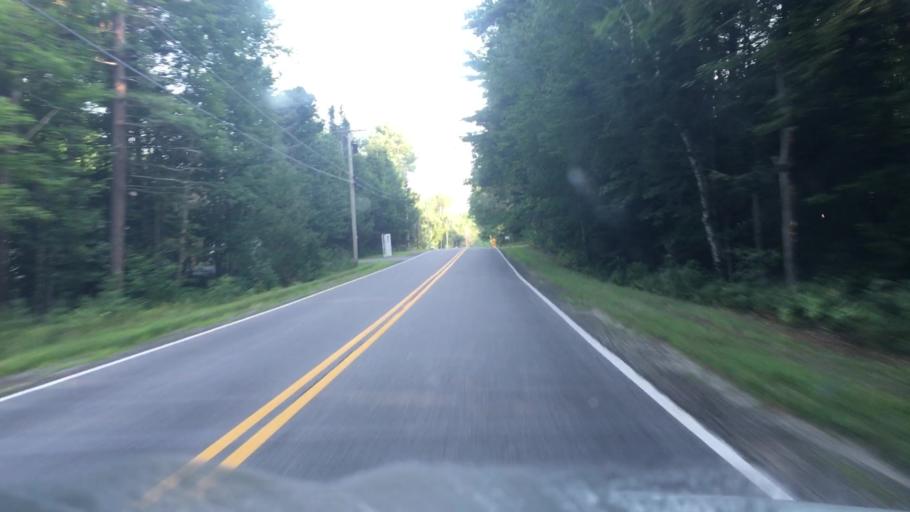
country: US
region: Maine
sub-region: Cumberland County
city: Freeport
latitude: 43.9197
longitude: -70.0909
